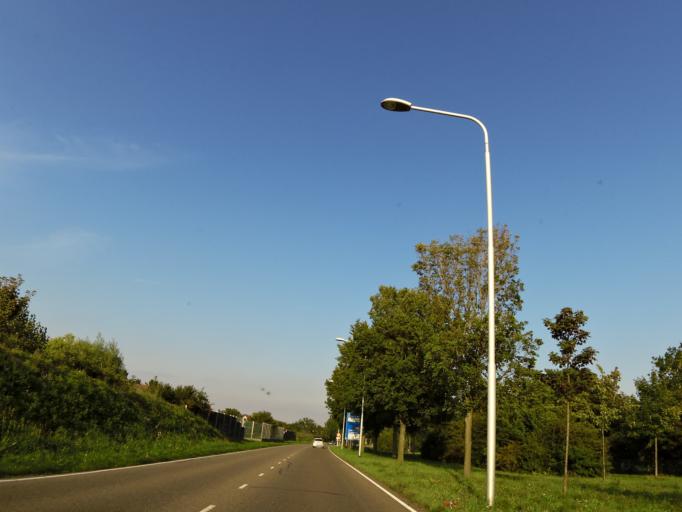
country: NL
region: Zeeland
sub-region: Gemeente Vlissingen
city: Vlissingen
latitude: 51.4597
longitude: 3.5650
